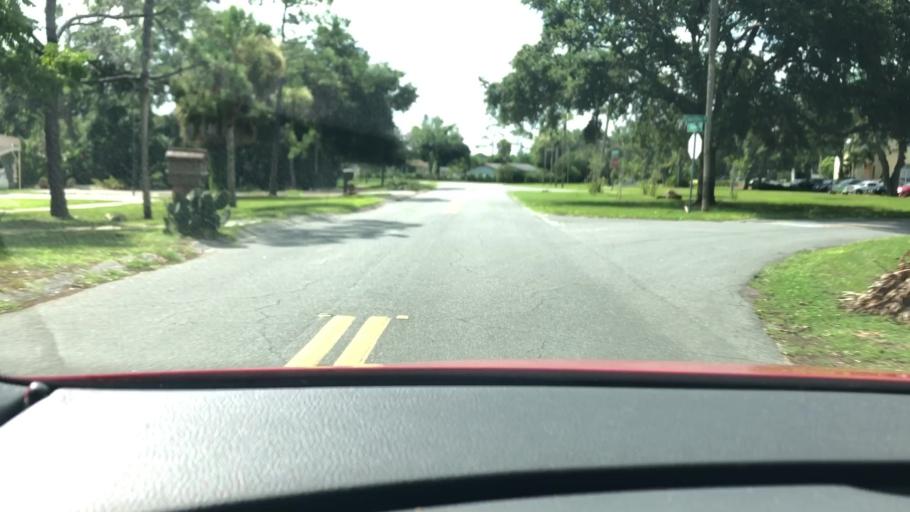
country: US
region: Florida
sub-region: Volusia County
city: Holly Hill
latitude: 29.2631
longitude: -81.0492
